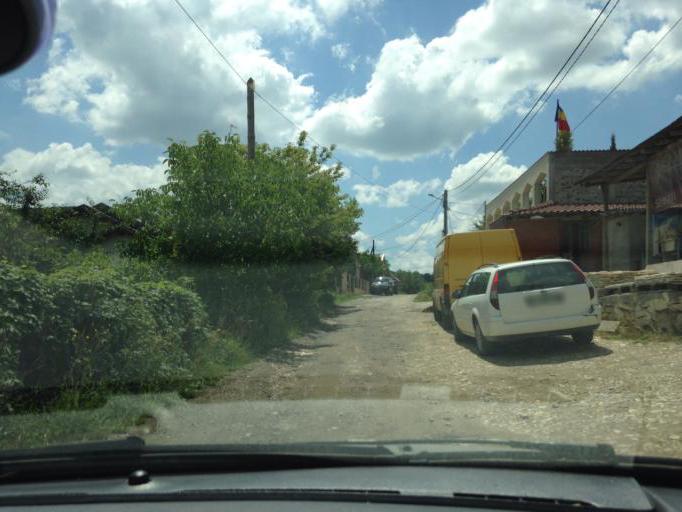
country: RO
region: Cluj
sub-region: Comuna Floresti
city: Floresti
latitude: 46.7431
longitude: 23.5322
